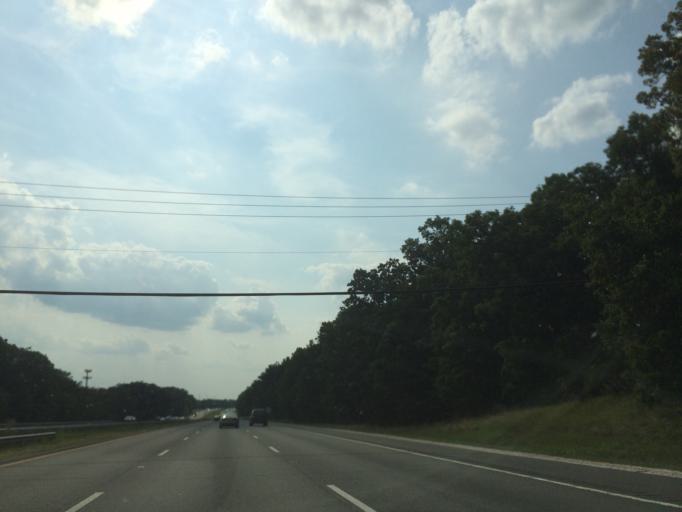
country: US
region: Maryland
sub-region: Baltimore County
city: Woodlawn
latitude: 39.3081
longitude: -76.7600
